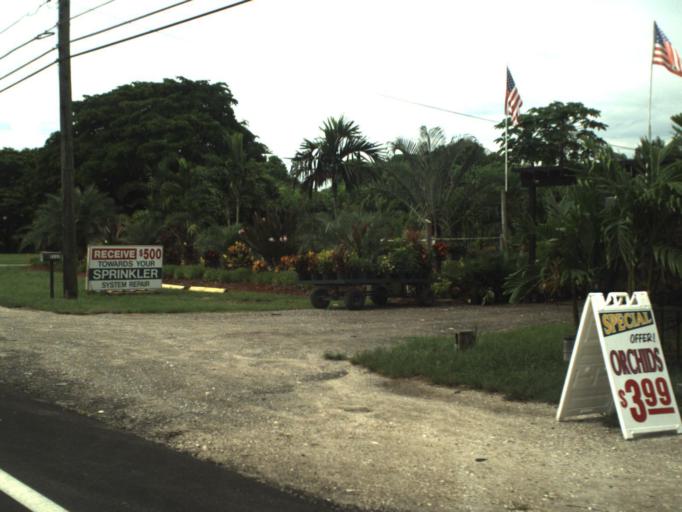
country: US
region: Florida
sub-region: Miami-Dade County
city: Richmond West
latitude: 25.5692
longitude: -80.4783
